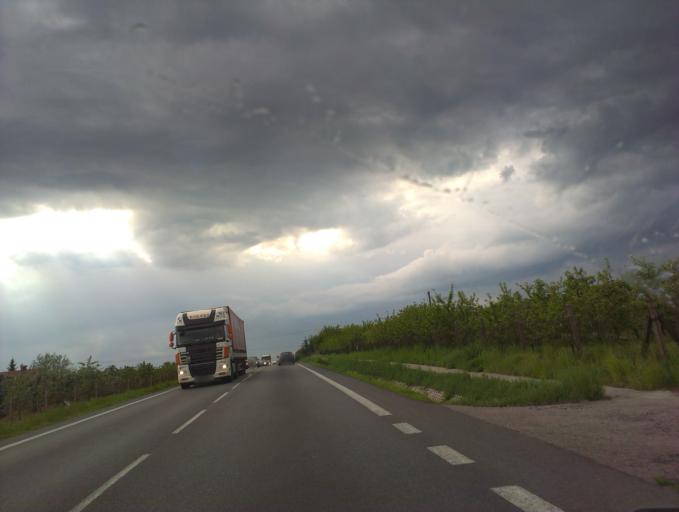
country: PL
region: Masovian Voivodeship
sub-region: Powiat grojecki
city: Pniewy
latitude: 51.9011
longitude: 20.7670
